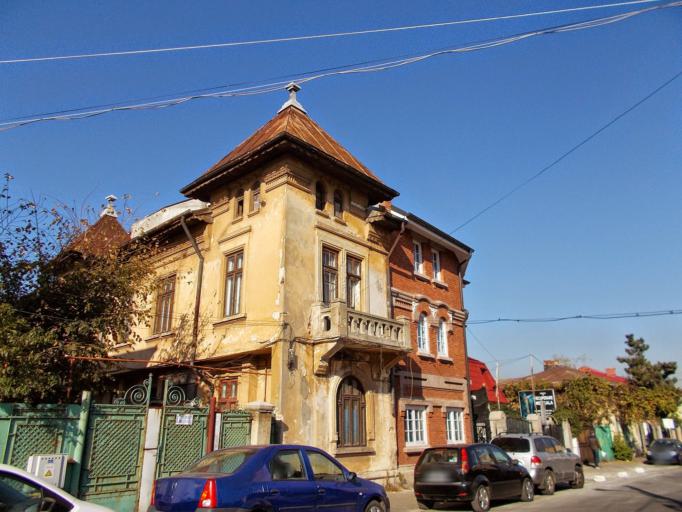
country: RO
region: Bucuresti
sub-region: Municipiul Bucuresti
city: Bucuresti
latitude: 44.4172
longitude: 26.1068
